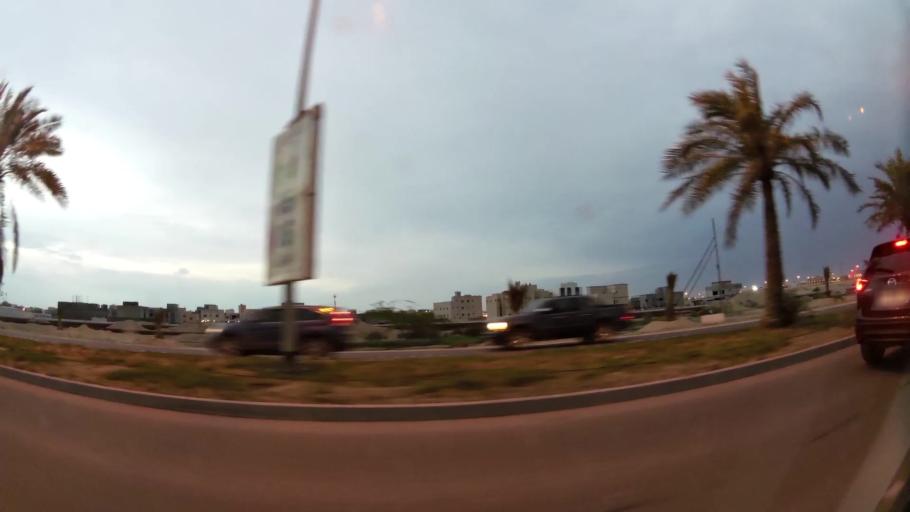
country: BH
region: Central Governorate
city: Madinat Hamad
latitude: 26.1415
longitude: 50.5042
